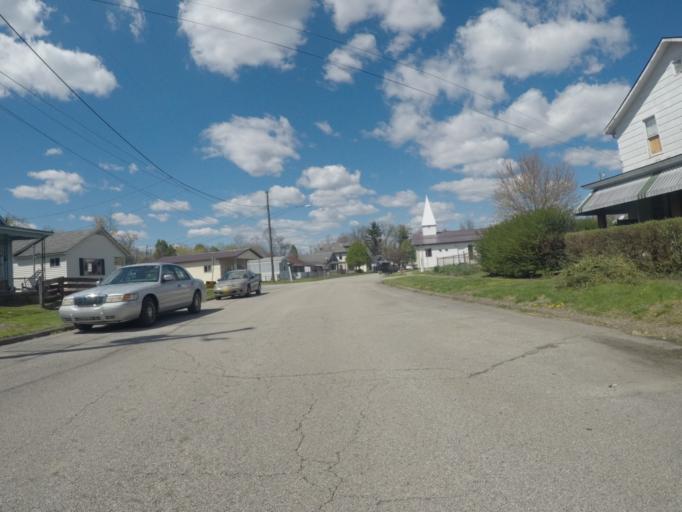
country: US
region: West Virginia
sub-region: Wayne County
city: Kenova
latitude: 38.3946
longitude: -82.5762
